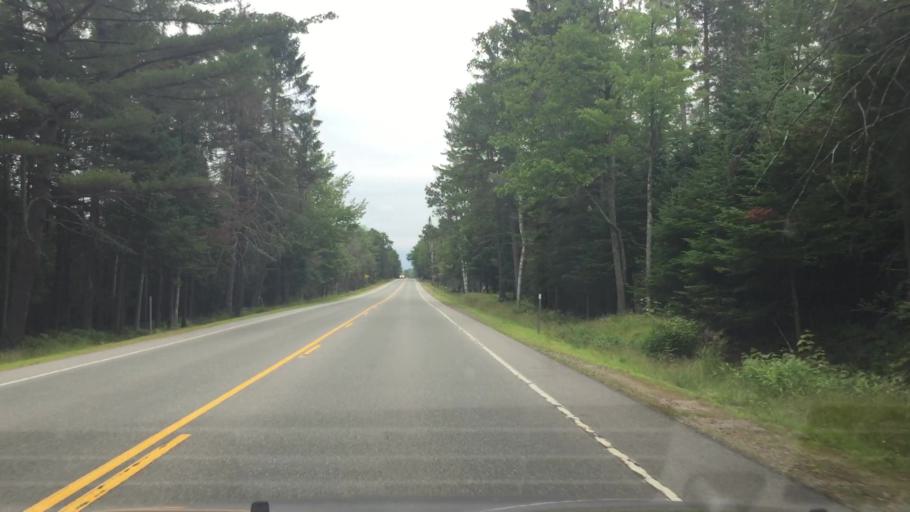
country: US
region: New Hampshire
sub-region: Grafton County
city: Deerfield
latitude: 44.2451
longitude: -71.6283
